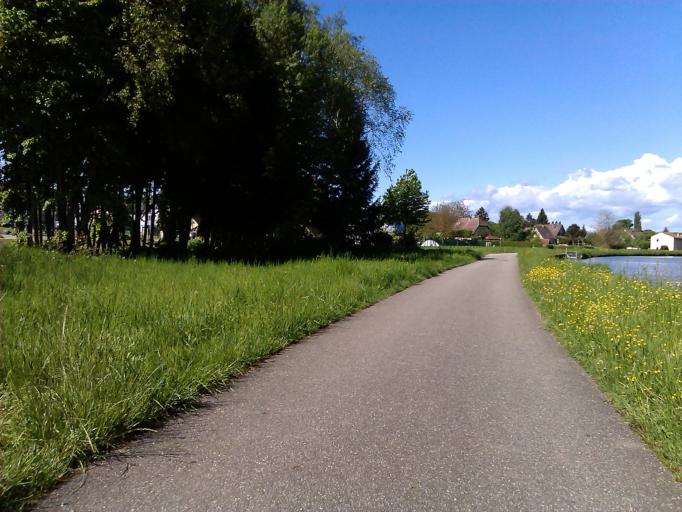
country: FR
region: Alsace
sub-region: Departement du Haut-Rhin
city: Dannemarie
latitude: 47.6319
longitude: 7.1008
